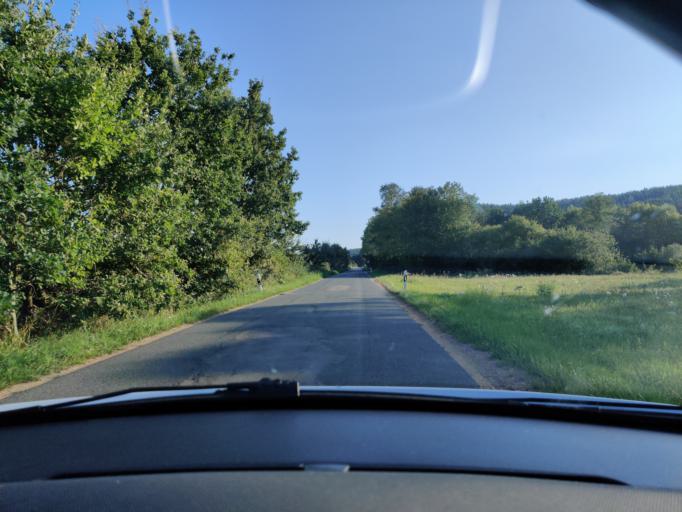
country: DE
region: Bavaria
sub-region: Upper Palatinate
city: Nabburg
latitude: 49.4379
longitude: 12.1722
